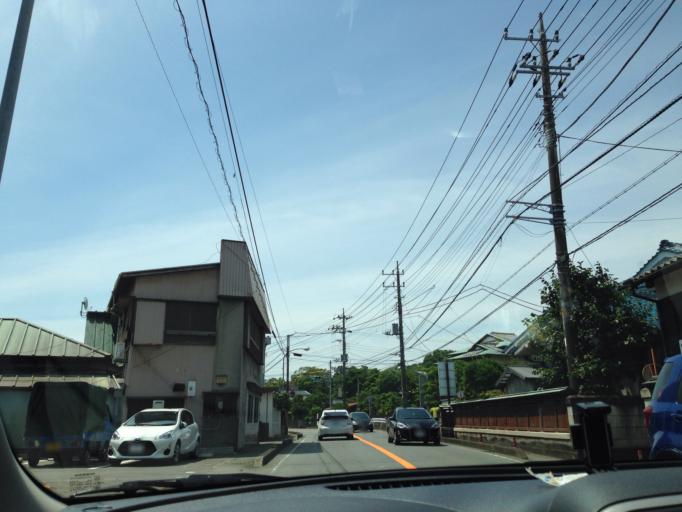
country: JP
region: Shizuoka
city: Numazu
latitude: 35.0741
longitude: 138.8732
